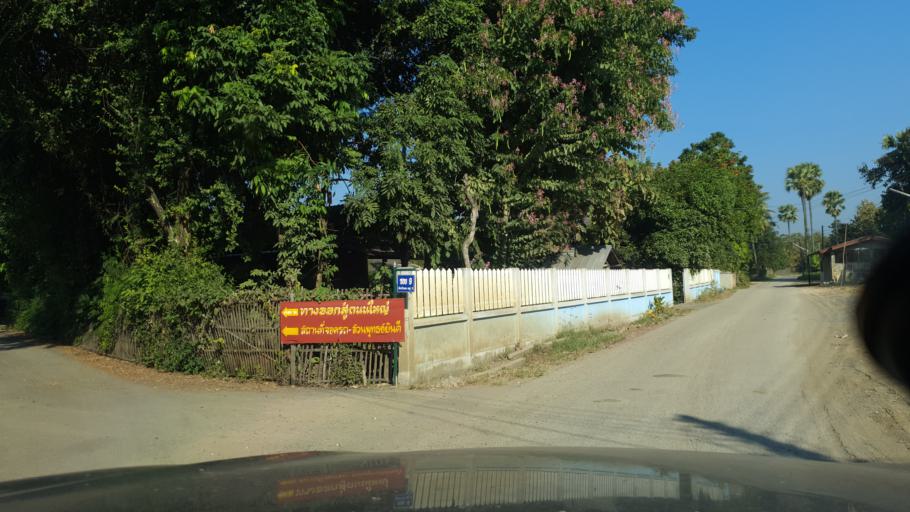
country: TH
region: Chiang Mai
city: San Kamphaeng
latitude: 18.7447
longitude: 99.1714
